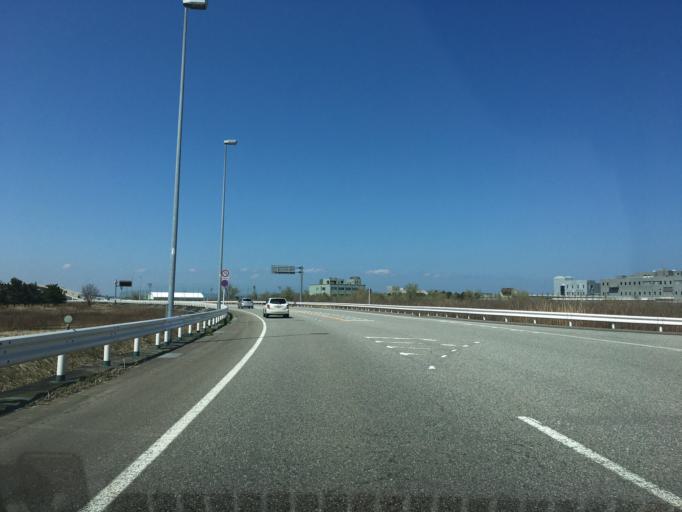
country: JP
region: Toyama
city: Kuragaki-kosugi
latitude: 36.7719
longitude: 137.1334
